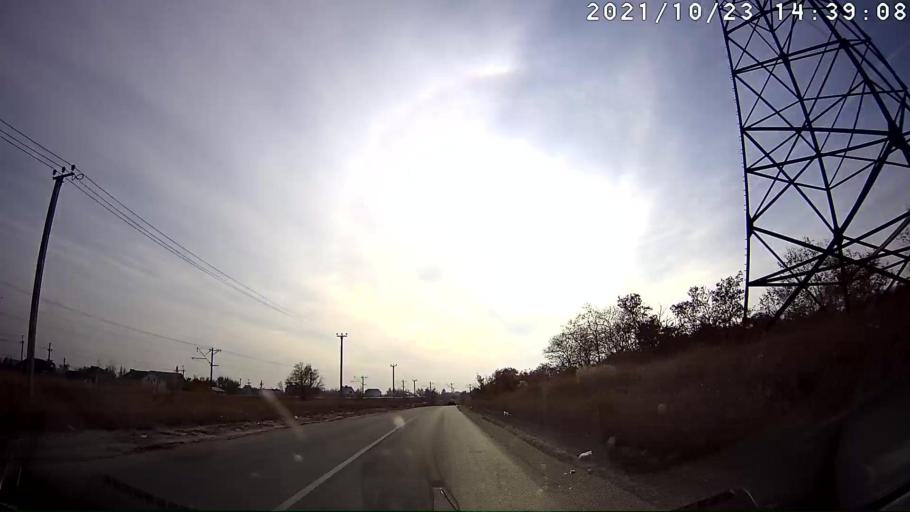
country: RU
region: Volgograd
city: Krasnoslobodsk
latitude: 48.4865
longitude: 44.5465
